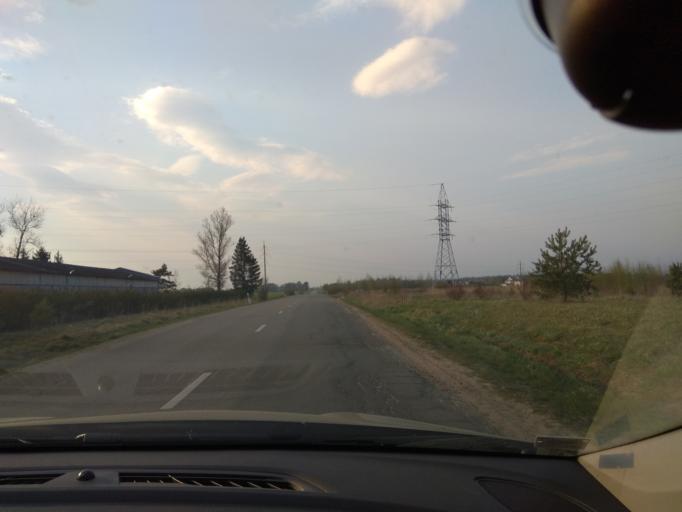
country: LT
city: Lentvaris
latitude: 54.6130
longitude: 25.1201
